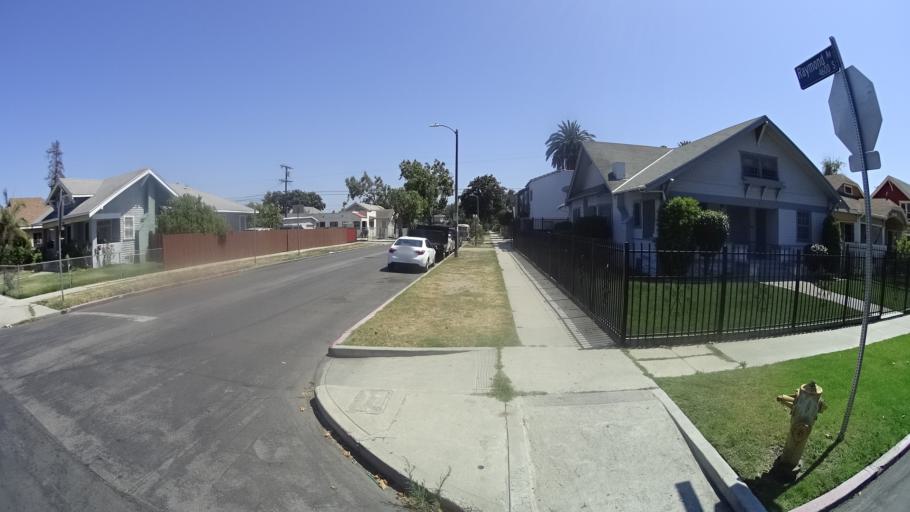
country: US
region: California
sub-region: Los Angeles County
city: View Park-Windsor Hills
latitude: 34.0016
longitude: -118.2981
